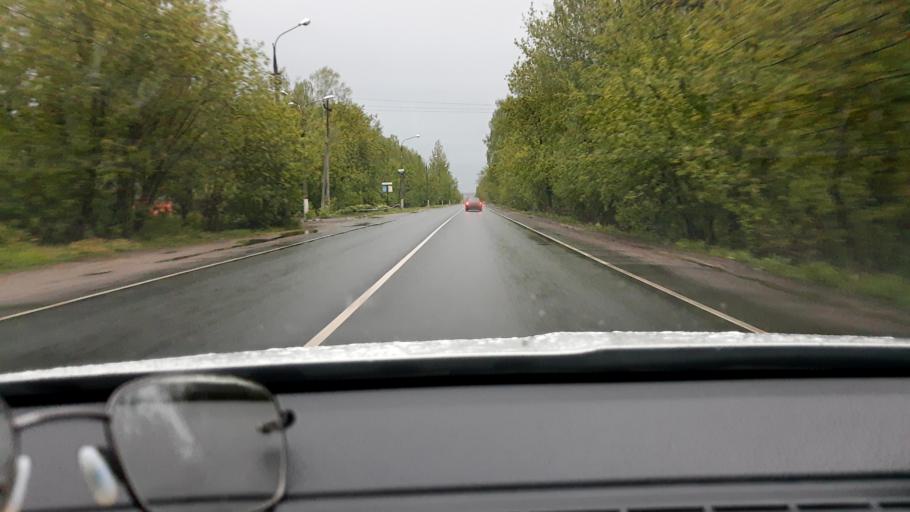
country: RU
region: Moskovskaya
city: Zagoryanskiy
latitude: 55.9274
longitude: 37.9222
